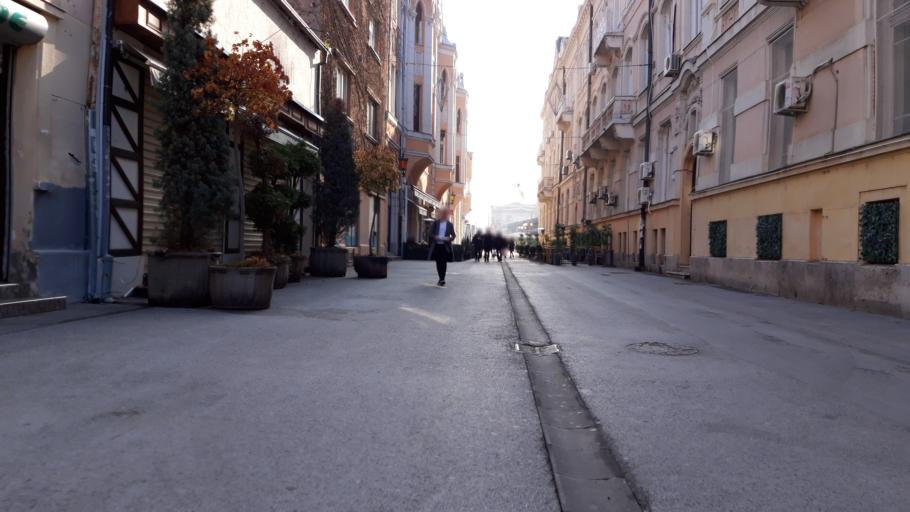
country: RS
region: Autonomna Pokrajina Vojvodina
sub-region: Juznobacki Okrug
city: Novi Sad
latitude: 45.2560
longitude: 19.8444
